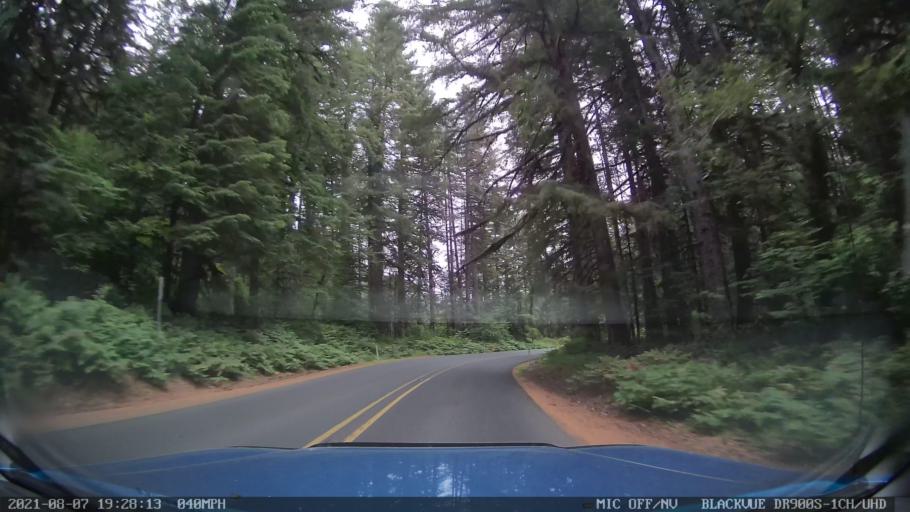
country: US
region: Oregon
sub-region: Linn County
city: Lyons
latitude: 44.8832
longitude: -122.6412
